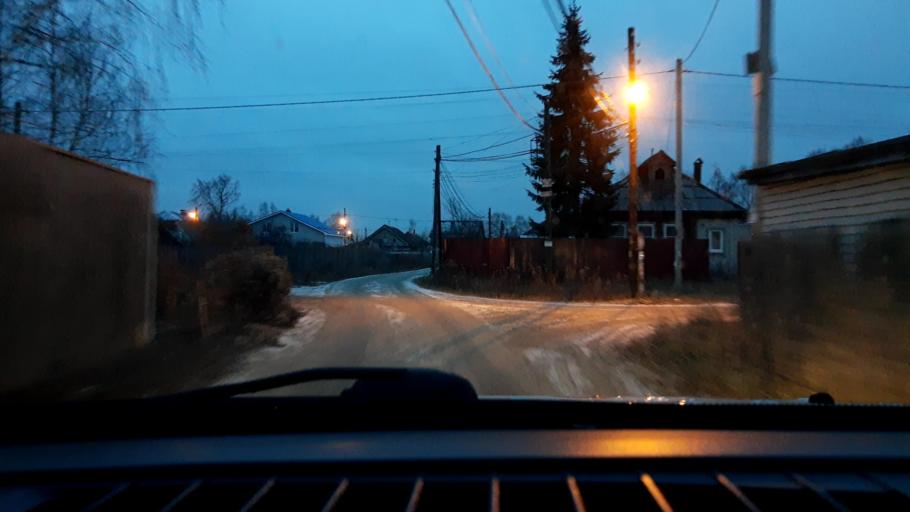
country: RU
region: Nizjnij Novgorod
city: Gorbatovka
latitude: 56.3882
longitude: 43.7518
